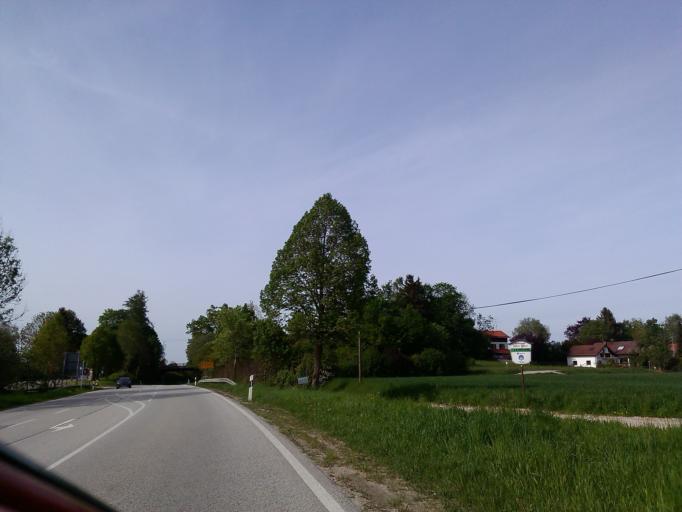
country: DE
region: Bavaria
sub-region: Upper Bavaria
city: Feldafing
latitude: 47.9420
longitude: 11.2611
